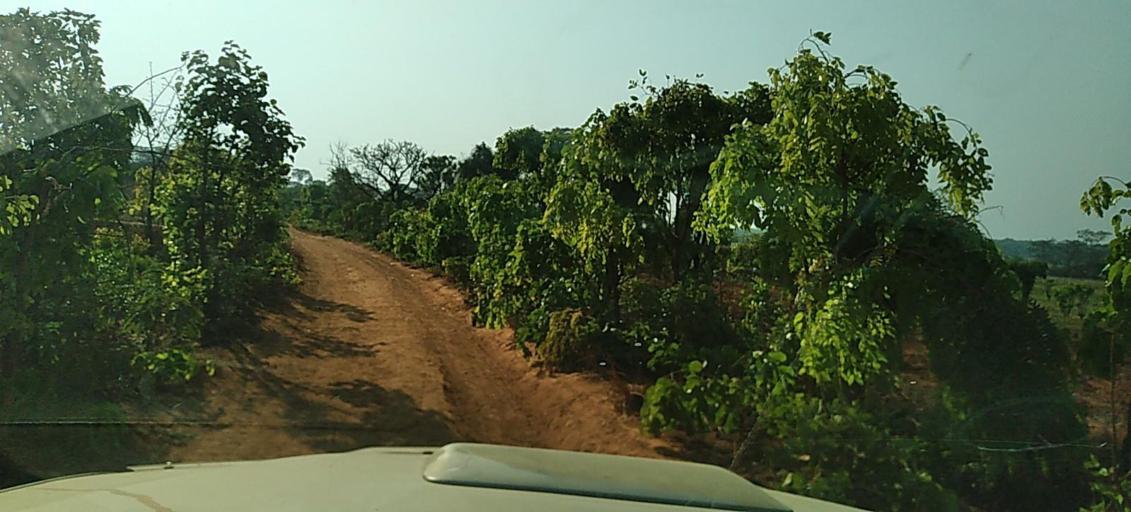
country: ZM
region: North-Western
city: Kasempa
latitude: -13.1838
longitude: 25.9515
